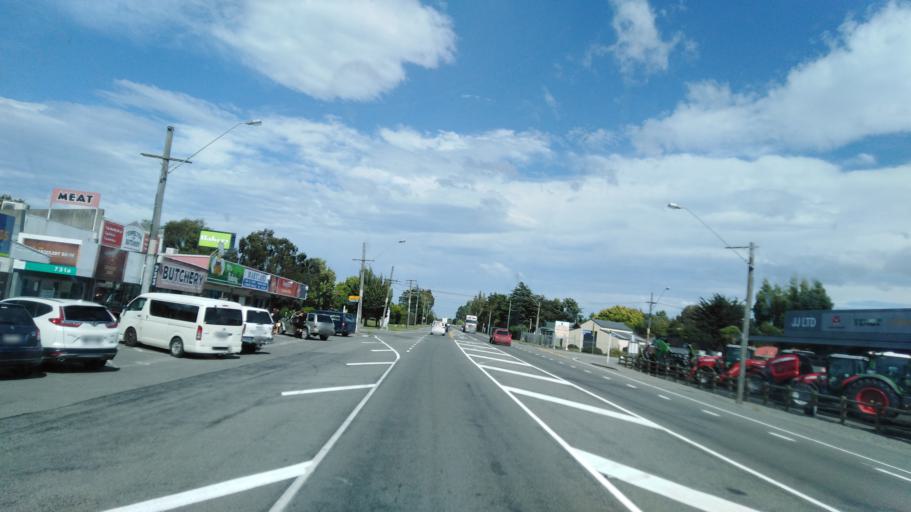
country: NZ
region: Canterbury
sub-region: Selwyn District
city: Prebbleton
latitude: -43.5501
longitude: 172.4876
